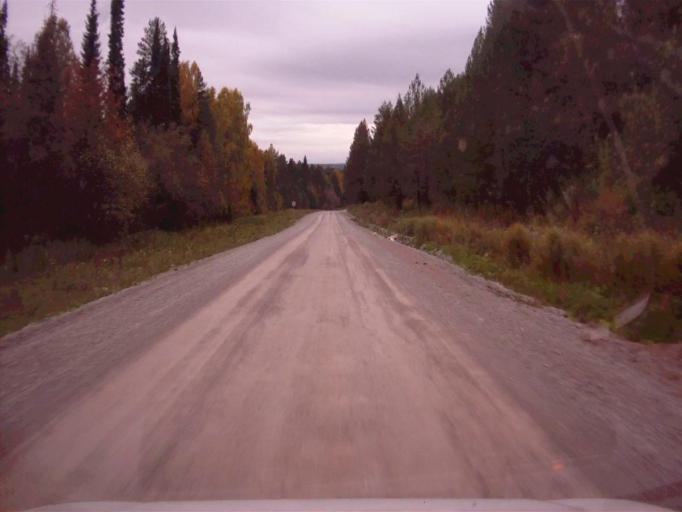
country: RU
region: Chelyabinsk
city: Nyazepetrovsk
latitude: 56.0511
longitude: 59.5322
